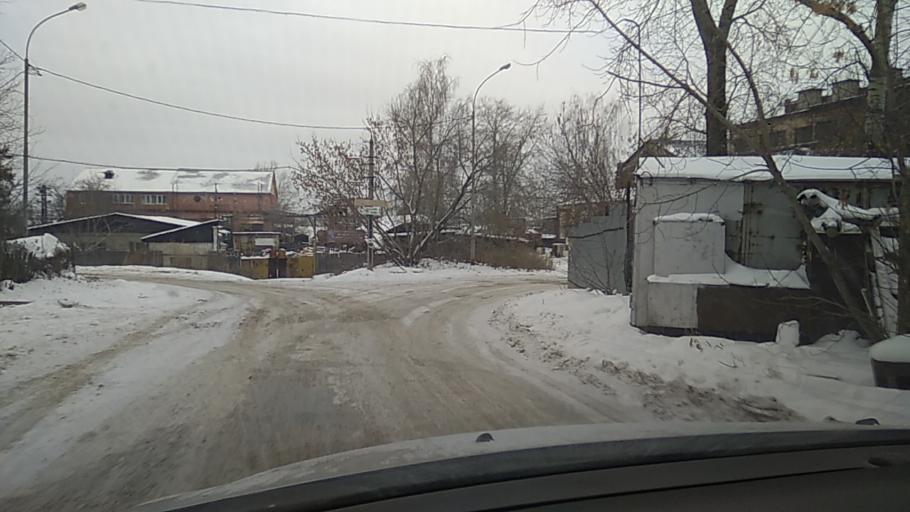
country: RU
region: Sverdlovsk
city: Shirokaya Rechka
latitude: 56.8474
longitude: 60.4996
